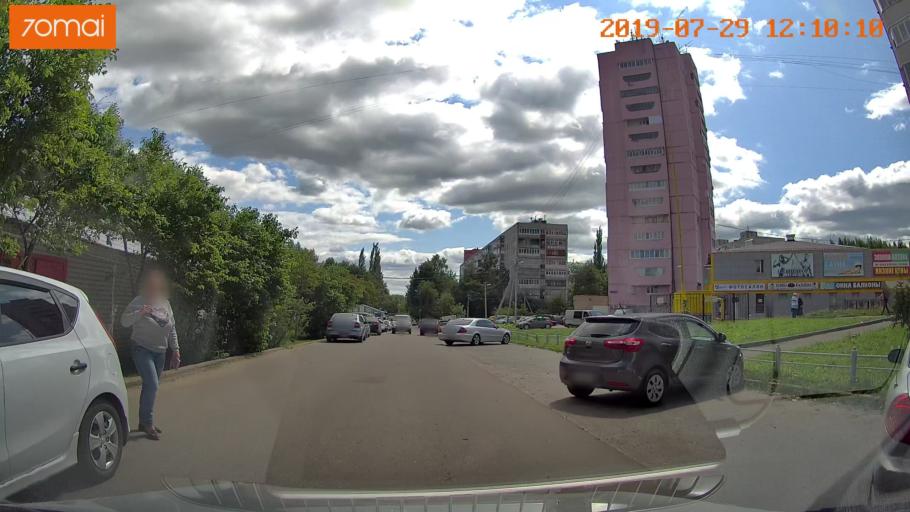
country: RU
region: Moskovskaya
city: Voskresensk
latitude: 55.3158
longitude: 38.6490
